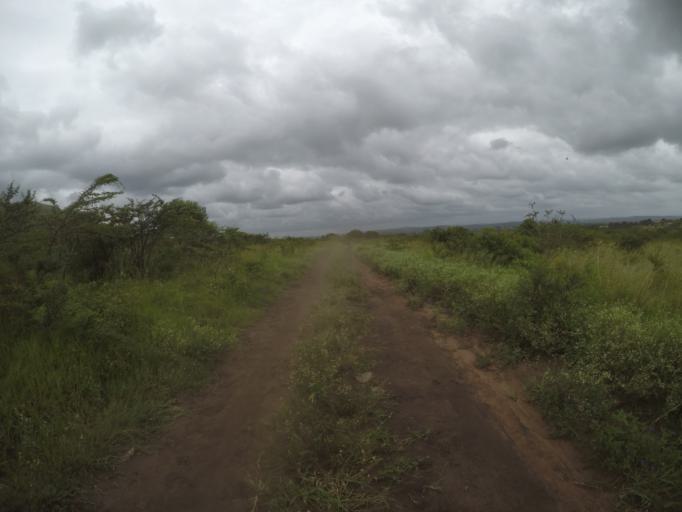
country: ZA
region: KwaZulu-Natal
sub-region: uThungulu District Municipality
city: Empangeni
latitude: -28.5588
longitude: 31.8840
